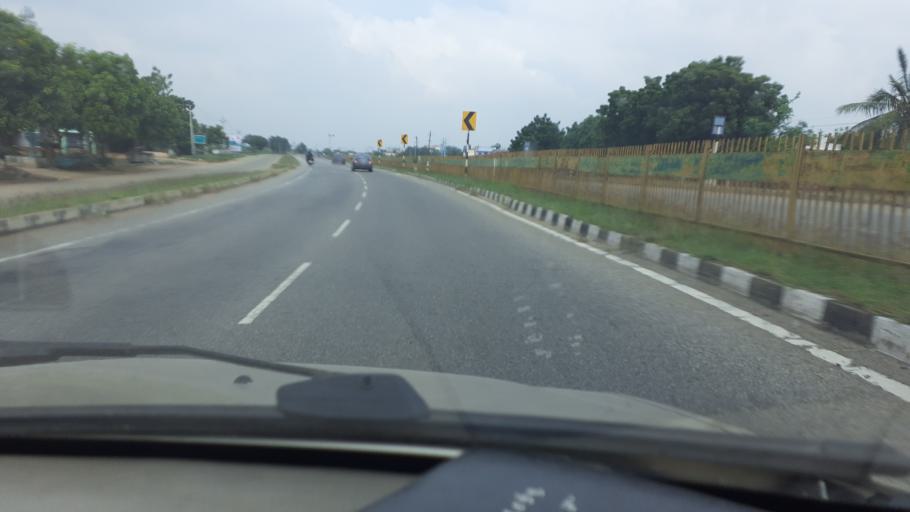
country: IN
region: Tamil Nadu
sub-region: Tirunelveli Kattabo
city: Nanguneri
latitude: 8.4540
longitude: 77.6516
